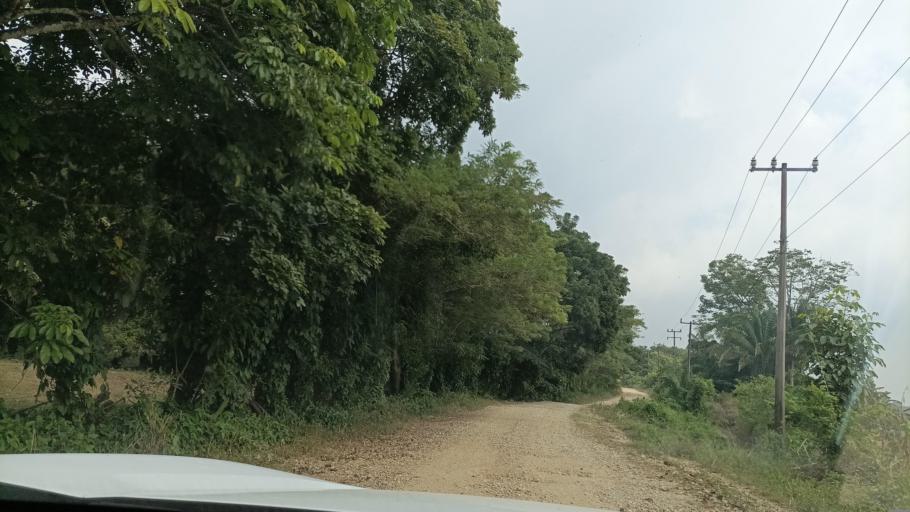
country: MX
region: Veracruz
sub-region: Moloacan
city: Cuichapa
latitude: 17.5872
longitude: -94.2052
